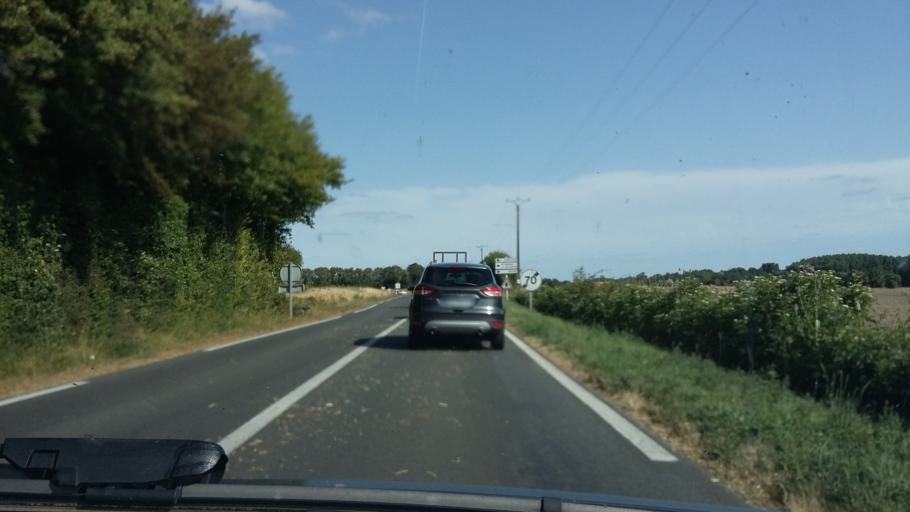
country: FR
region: Poitou-Charentes
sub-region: Departement de la Charente-Maritime
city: Saint-Jean-d'Angely
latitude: 45.9228
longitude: -0.4553
